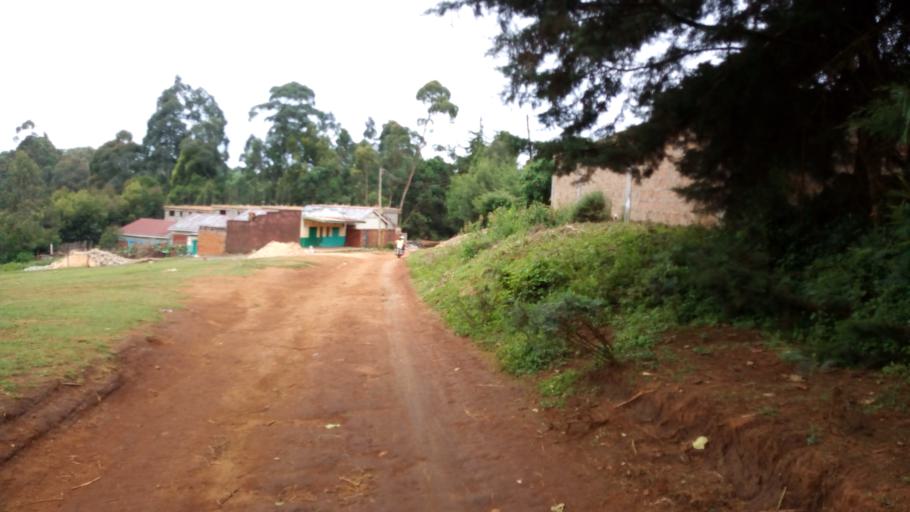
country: KE
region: Makueni
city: Wote
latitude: -1.6584
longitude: 37.4548
